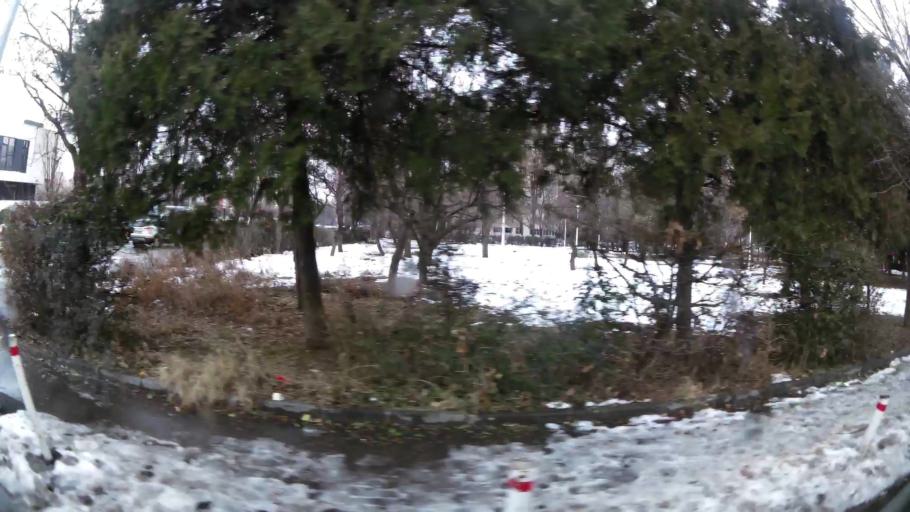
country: RO
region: Ilfov
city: Dobroesti
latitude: 44.4176
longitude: 26.1716
